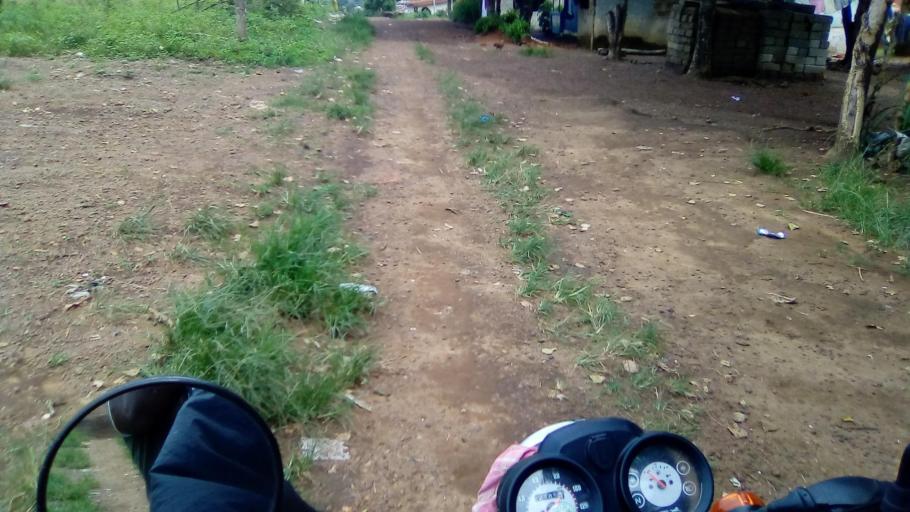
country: SL
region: Southern Province
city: Bo
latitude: 7.9332
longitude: -11.7213
